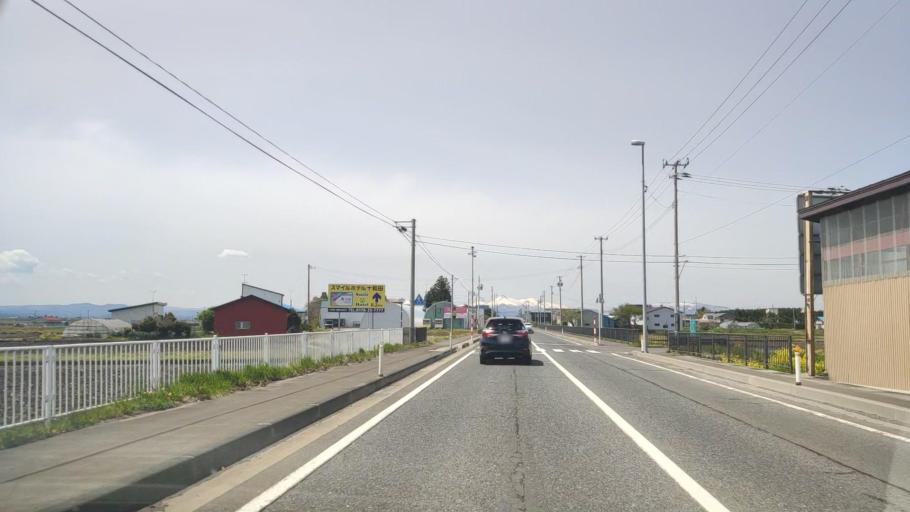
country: JP
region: Aomori
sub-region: Misawa Shi
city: Inuotose
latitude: 40.6101
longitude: 141.2789
